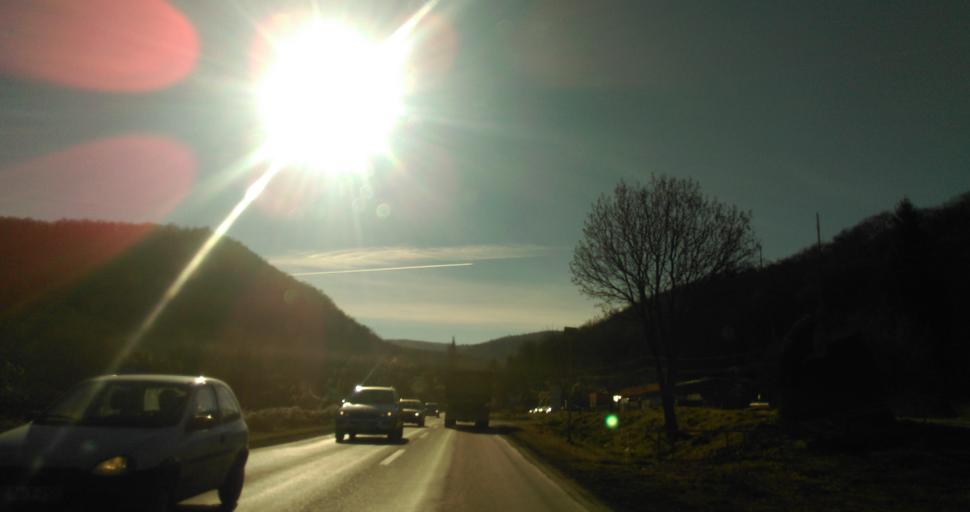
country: RS
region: Autonomna Pokrajina Vojvodina
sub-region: Juznobacki Okrug
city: Novi Sad
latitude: 45.1882
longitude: 19.8403
